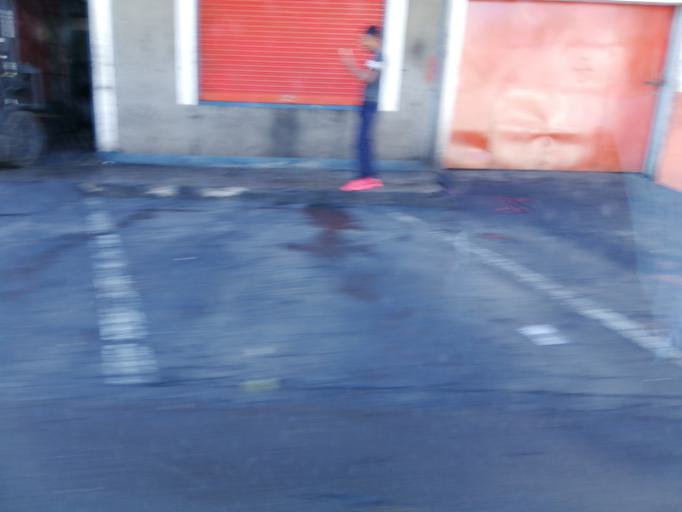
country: MU
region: Port Louis
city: Port Louis
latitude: -20.1618
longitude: 57.4901
